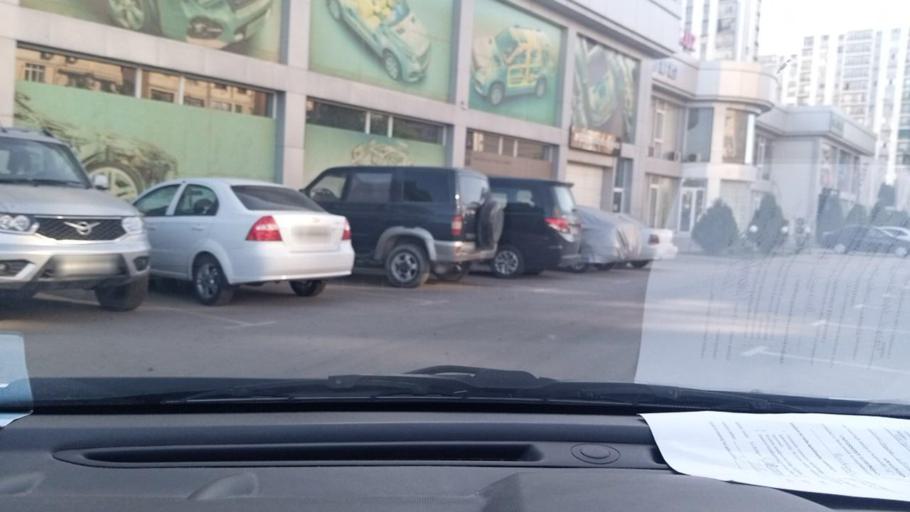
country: UZ
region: Toshkent
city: Salor
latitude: 41.3226
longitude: 69.3592
